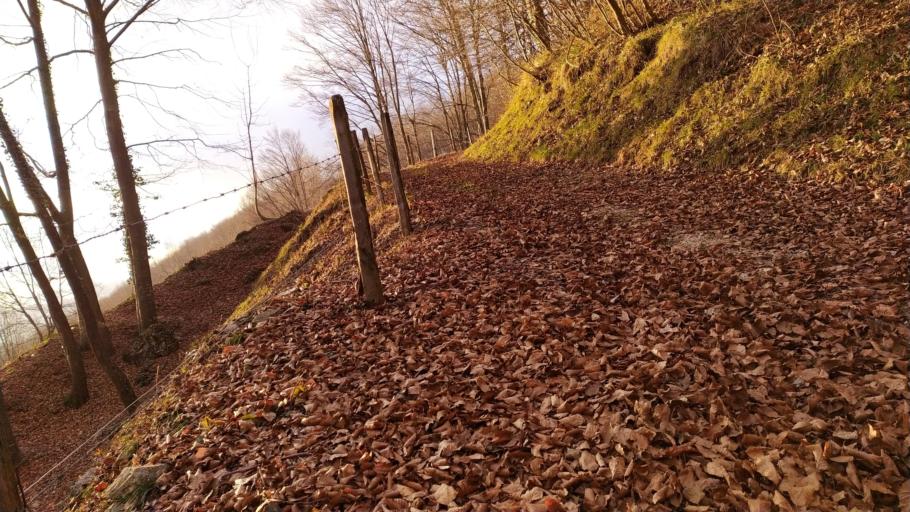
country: IT
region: Veneto
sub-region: Provincia di Vicenza
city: Velo d'Astico
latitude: 45.7650
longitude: 11.3672
